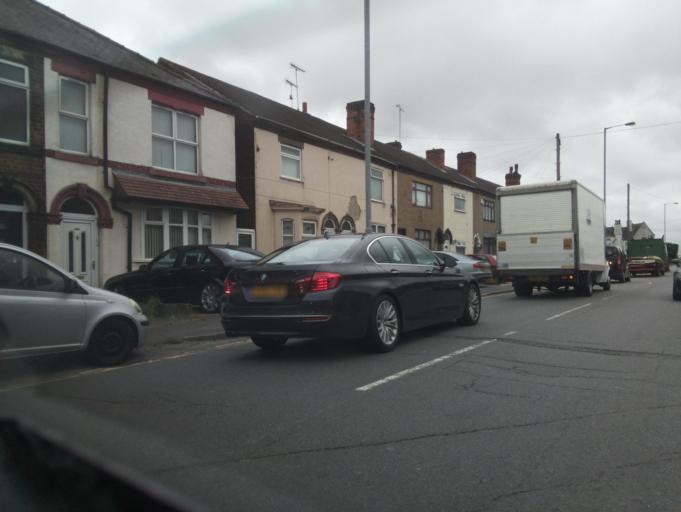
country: GB
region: England
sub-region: Staffordshire
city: Burton upon Trent
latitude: 52.8201
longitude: -1.6273
